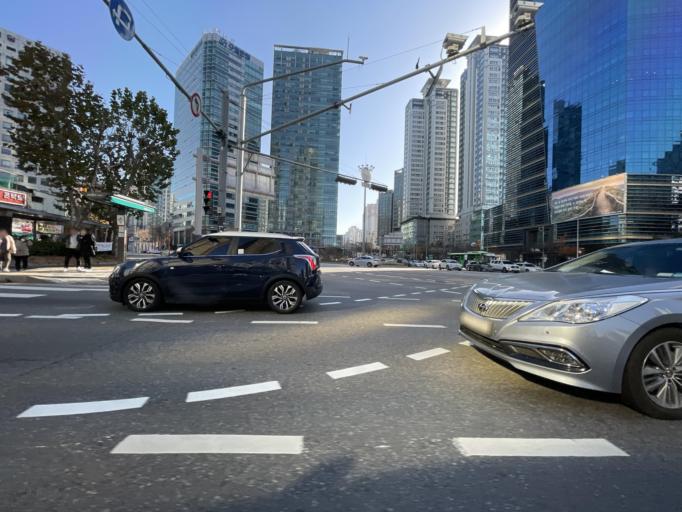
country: KR
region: Seoul
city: Seoul
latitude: 37.5441
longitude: 126.9513
